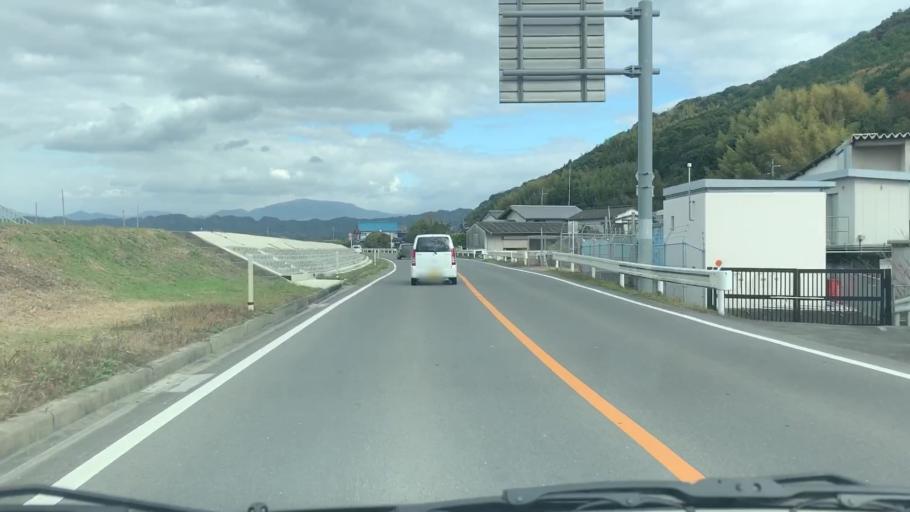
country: JP
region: Saga Prefecture
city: Takeocho-takeo
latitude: 33.2029
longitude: 130.0540
